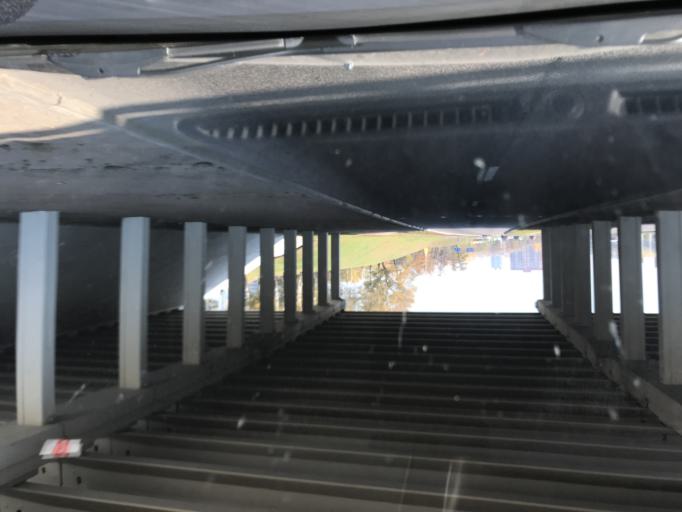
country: BY
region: Minsk
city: Vyaliki Trastsyanets
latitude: 53.8597
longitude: 27.6827
